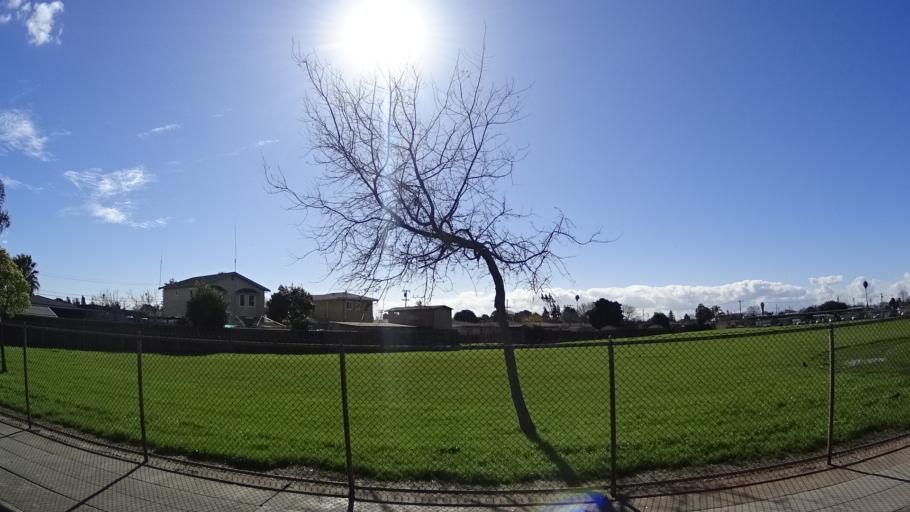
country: US
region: California
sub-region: Alameda County
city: San Lorenzo
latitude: 37.6749
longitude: -122.1166
